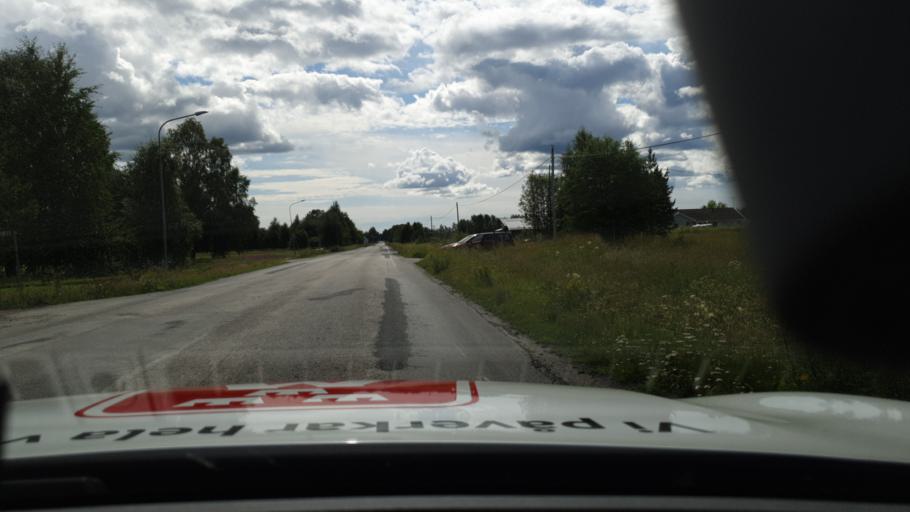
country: SE
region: Norrbotten
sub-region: Bodens Kommun
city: Boden
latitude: 65.8692
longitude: 21.6861
